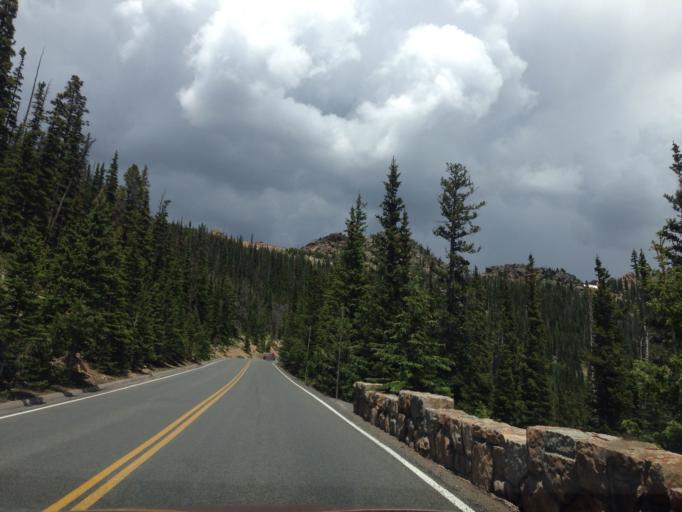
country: US
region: Colorado
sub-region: Larimer County
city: Estes Park
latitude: 40.3938
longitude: -105.6712
